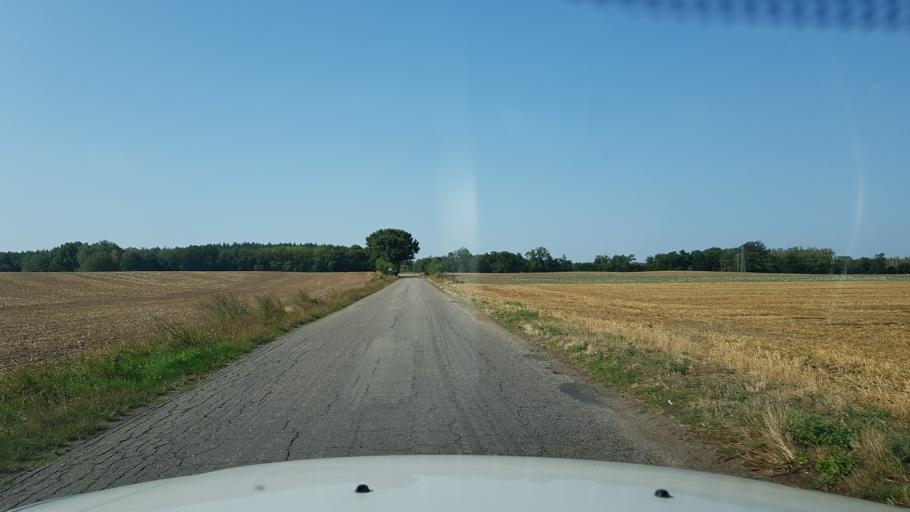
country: PL
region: West Pomeranian Voivodeship
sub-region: Powiat stargardzki
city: Dolice
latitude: 53.2307
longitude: 15.2162
